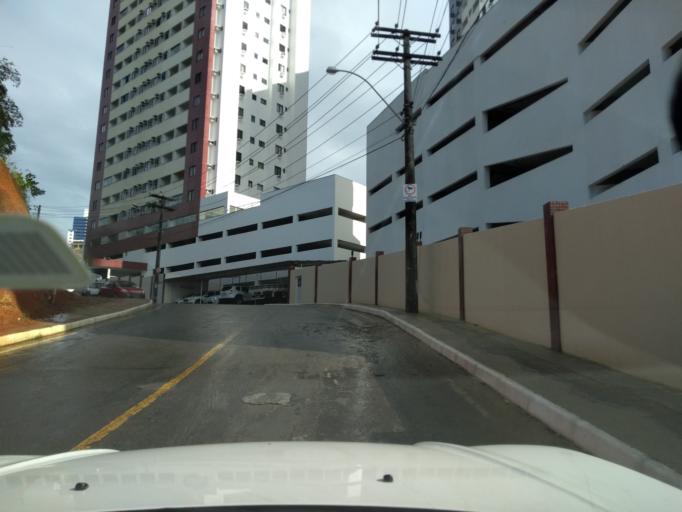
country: BR
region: Bahia
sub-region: Salvador
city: Salvador
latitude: -12.9743
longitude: -38.4783
